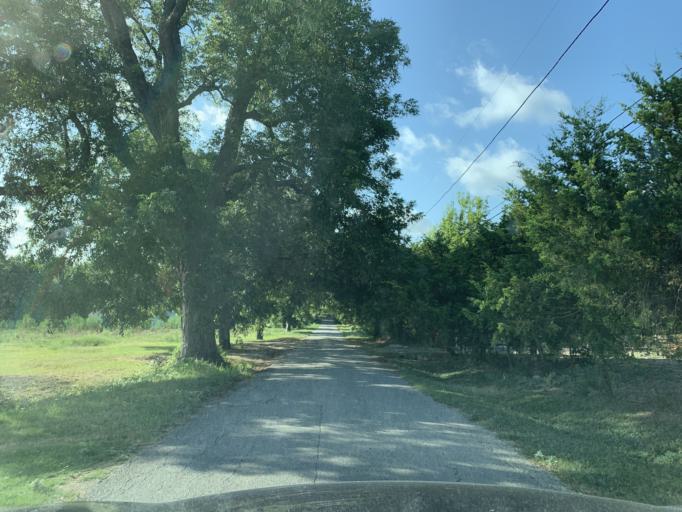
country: US
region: Texas
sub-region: Dallas County
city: Hutchins
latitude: 32.6771
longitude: -96.7735
